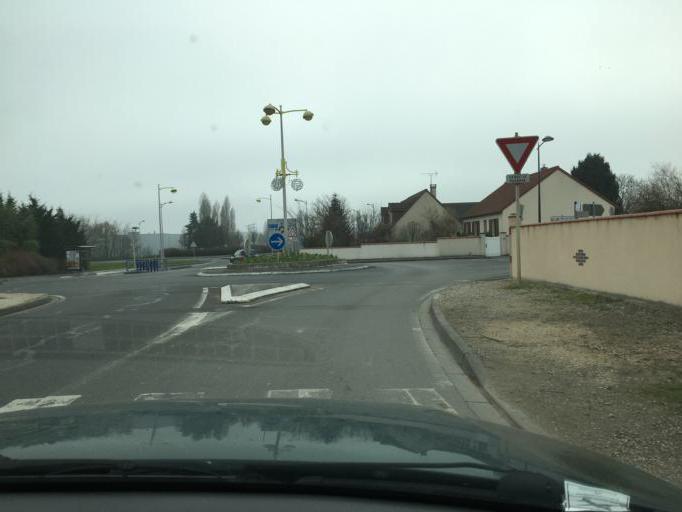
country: FR
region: Centre
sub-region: Departement du Loiret
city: Ormes
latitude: 47.9493
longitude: 1.8304
